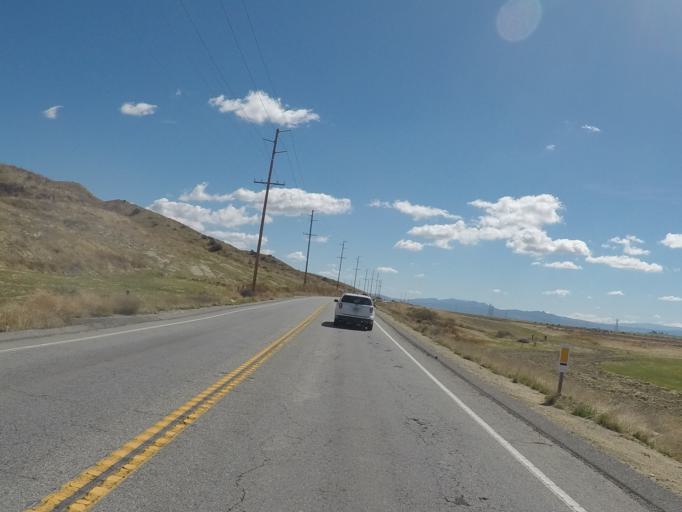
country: US
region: California
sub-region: Riverside County
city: Lakeview
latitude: 33.8754
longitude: -117.0515
